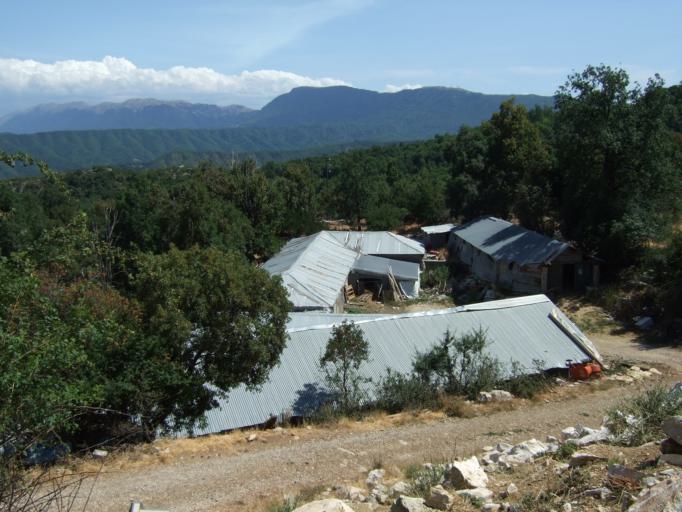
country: GR
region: Epirus
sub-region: Nomos Ioanninon
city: Asprangeloi
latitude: 39.8829
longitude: 20.7422
